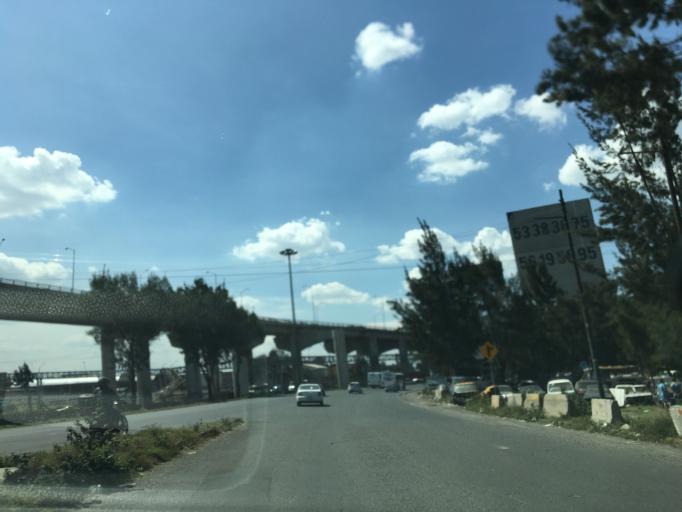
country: MX
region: Mexico
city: Los Reyes La Paz
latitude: 19.3599
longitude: -98.9977
